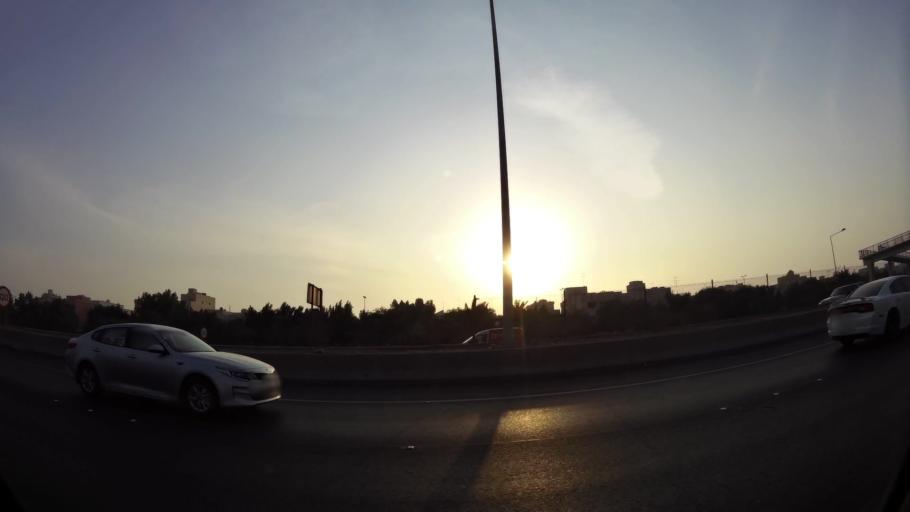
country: KW
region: Muhafazat Hawalli
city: Salwa
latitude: 29.2880
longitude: 48.0734
